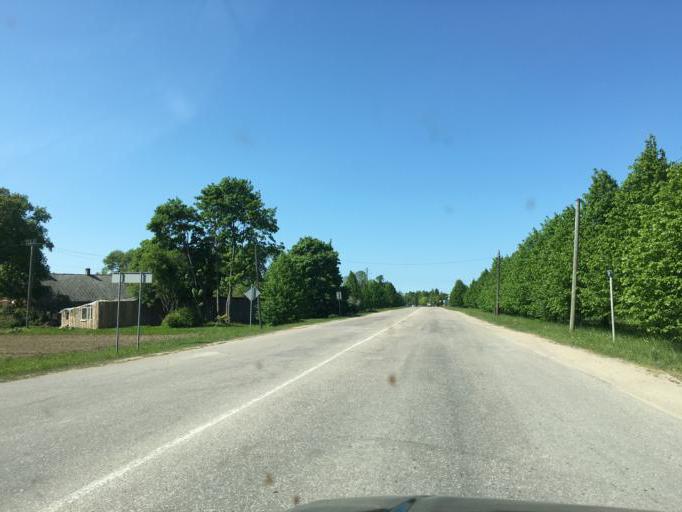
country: LV
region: Dundaga
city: Dundaga
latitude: 57.5001
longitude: 22.3530
